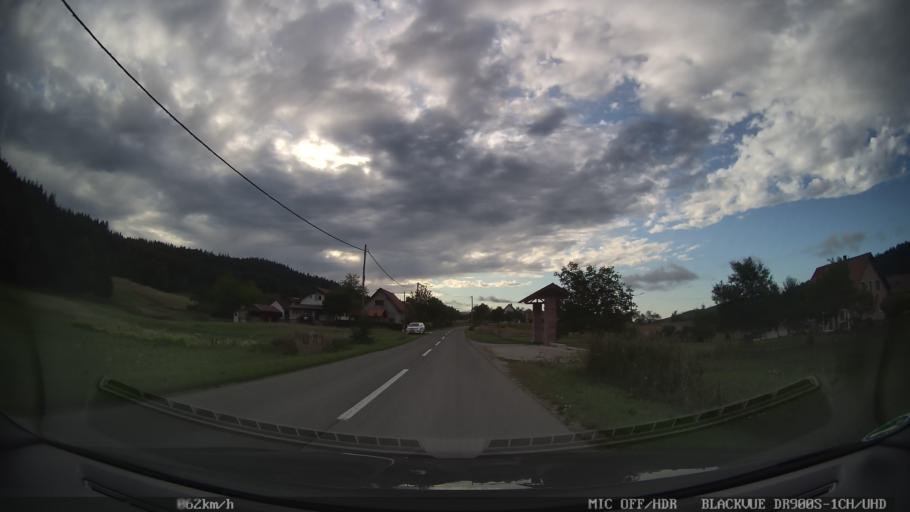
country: HR
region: Licko-Senjska
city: Jezerce
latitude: 44.9711
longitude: 15.5051
